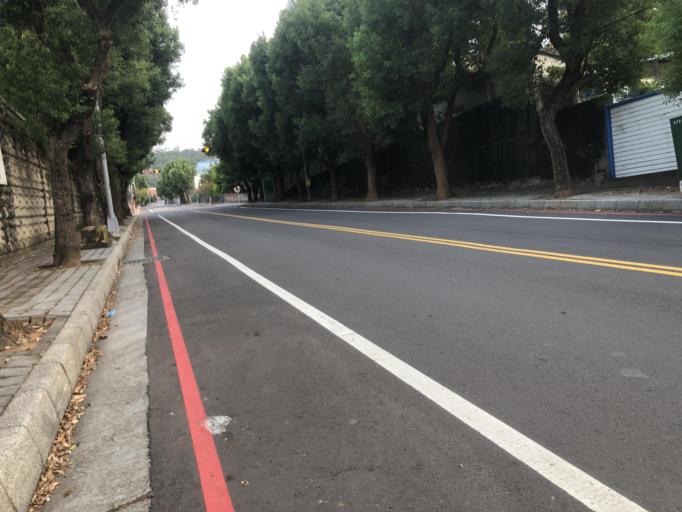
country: TW
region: Taiwan
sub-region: Miaoli
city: Miaoli
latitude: 24.4787
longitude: 120.7930
